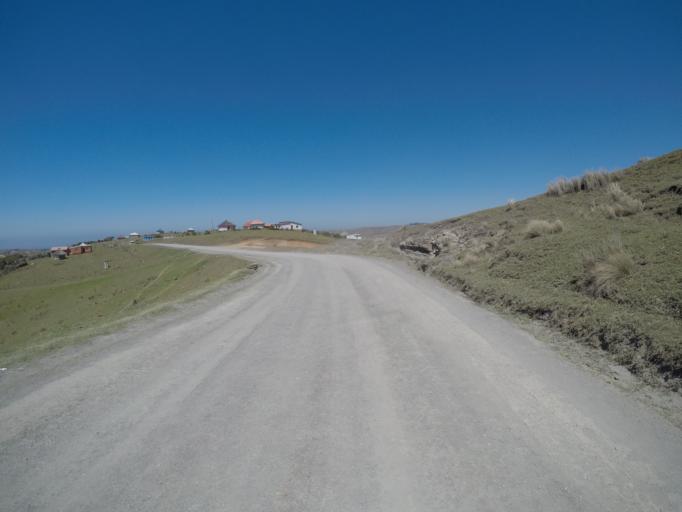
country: ZA
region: Eastern Cape
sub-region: OR Tambo District Municipality
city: Libode
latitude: -32.0150
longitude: 29.0773
